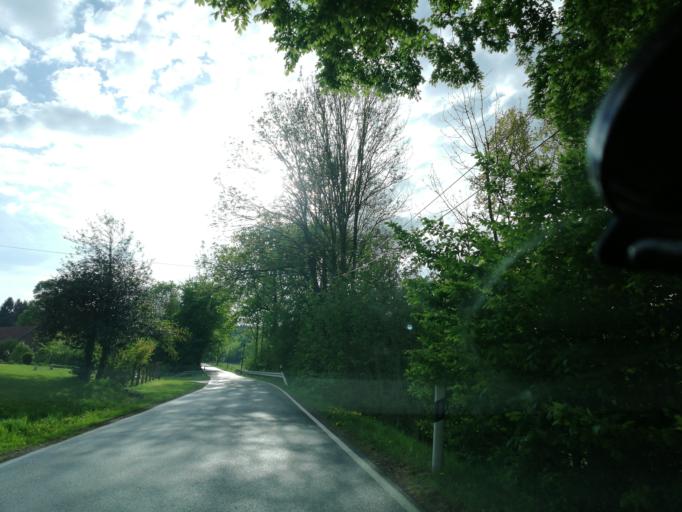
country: DE
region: Lower Saxony
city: Rinteln
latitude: 52.1313
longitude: 9.0323
